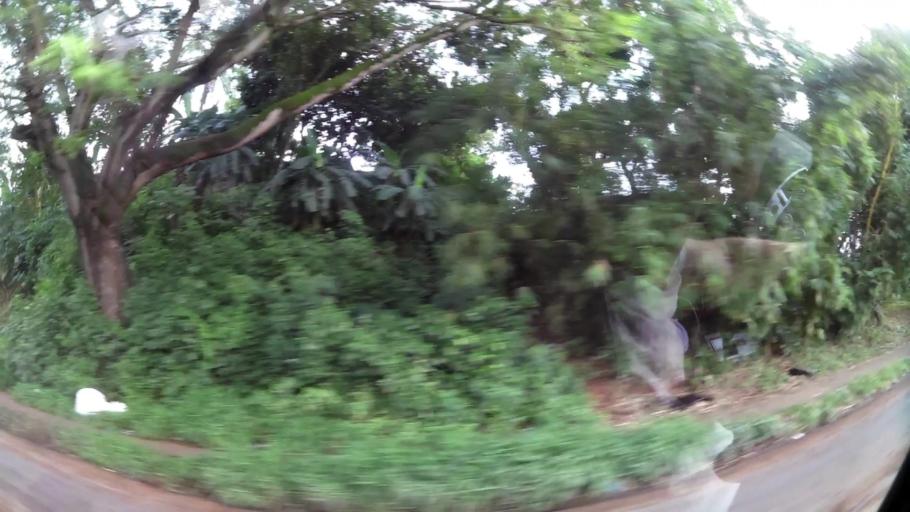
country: PA
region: Panama
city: Tocumen
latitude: 9.1006
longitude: -79.3680
